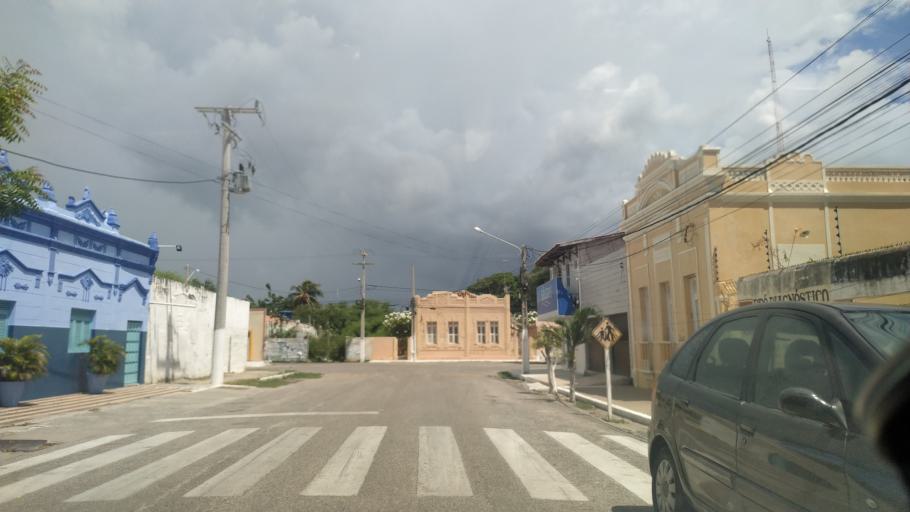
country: BR
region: Rio Grande do Norte
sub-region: Areia Branca
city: Areia Branca
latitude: -4.9578
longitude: -37.1362
